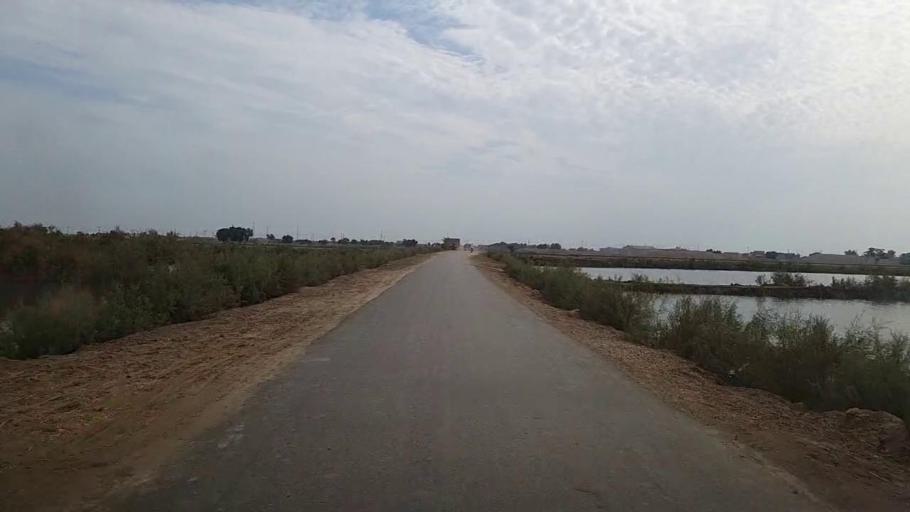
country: PK
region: Sindh
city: Thul
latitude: 28.2618
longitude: 68.7778
